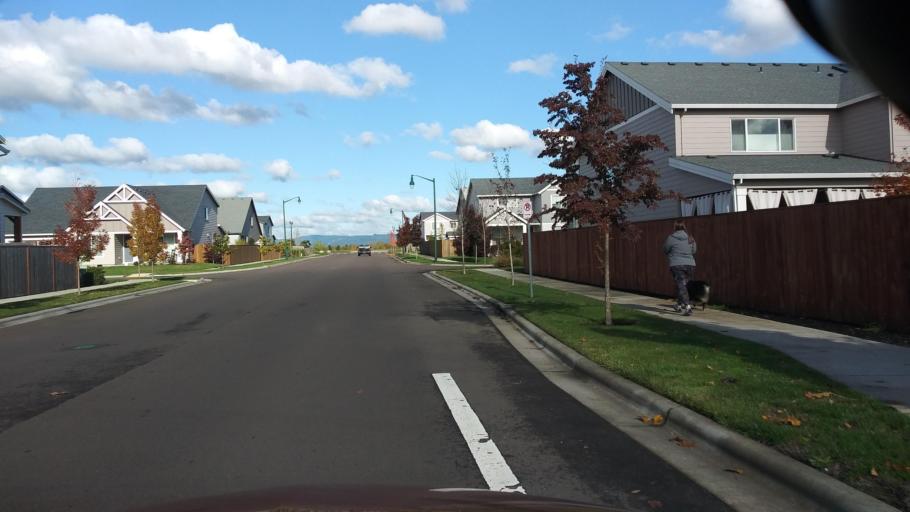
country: US
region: Oregon
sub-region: Washington County
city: Forest Grove
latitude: 45.5376
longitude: -123.1170
